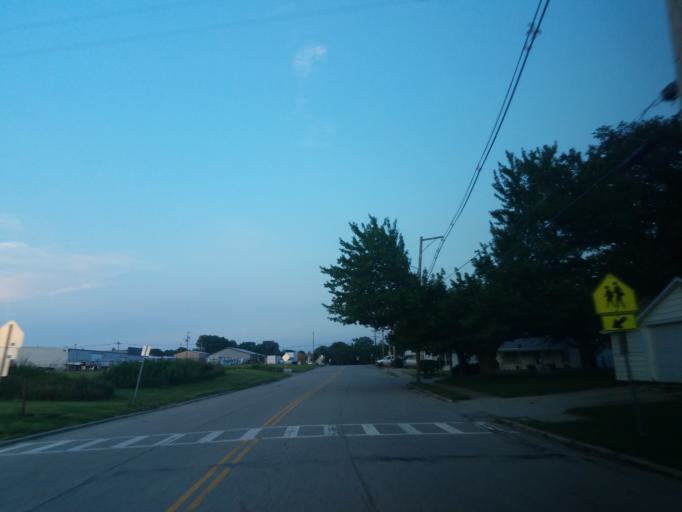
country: US
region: Illinois
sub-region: McLean County
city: Bloomington
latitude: 40.4416
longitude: -88.9934
